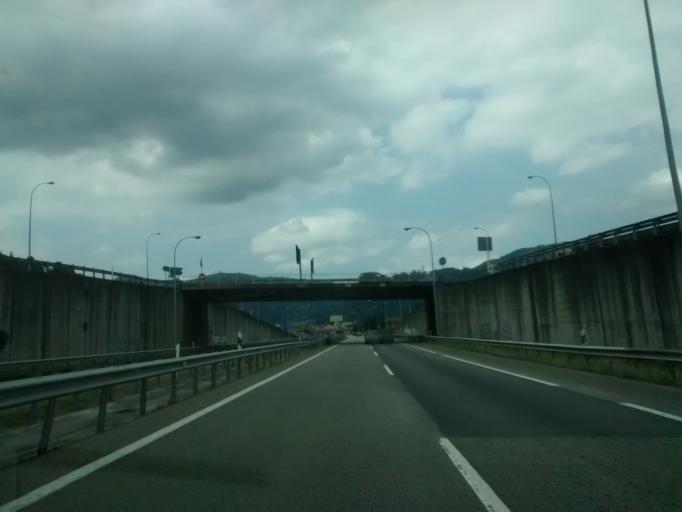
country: ES
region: Asturias
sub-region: Province of Asturias
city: Mieres
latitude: 43.2376
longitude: -5.7800
